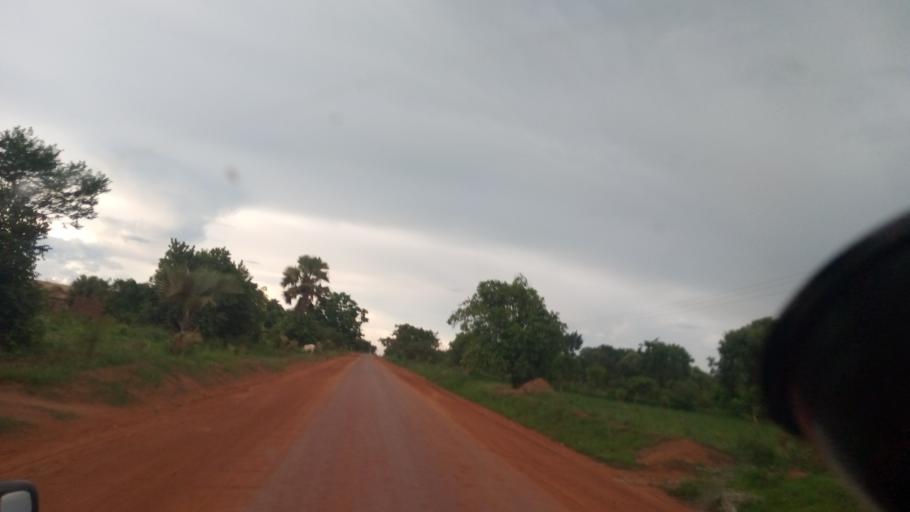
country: UG
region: Northern Region
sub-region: Kole District
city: Kole
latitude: 2.4713
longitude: 32.9364
